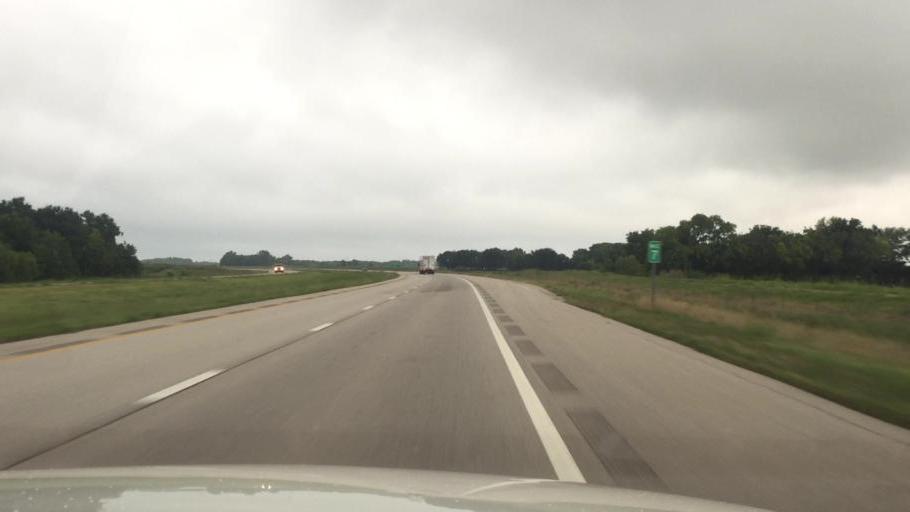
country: US
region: Kansas
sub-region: Montgomery County
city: Coffeyville
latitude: 37.0809
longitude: -95.5899
